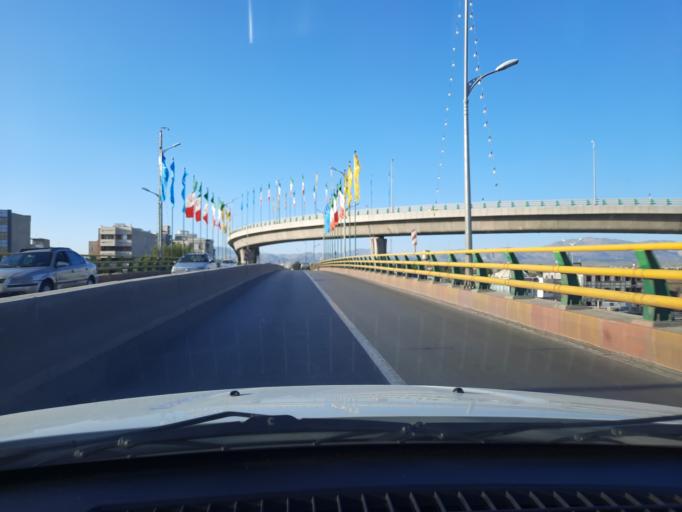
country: IR
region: Qazvin
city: Qazvin
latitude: 36.2736
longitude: 50.0235
